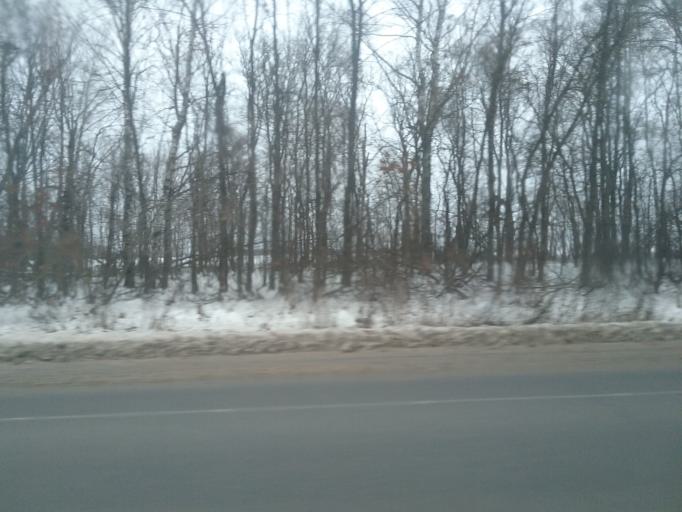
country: RU
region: Tula
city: Bolokhovo
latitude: 54.0463
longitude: 37.8521
